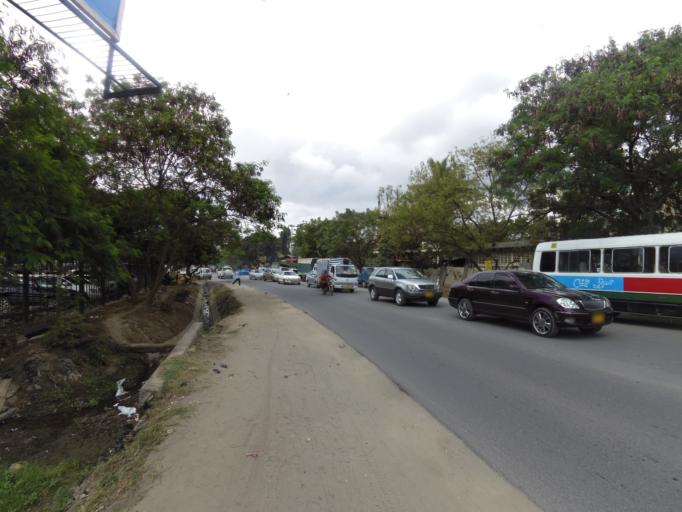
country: TZ
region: Dar es Salaam
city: Magomeni
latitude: -6.7747
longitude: 39.2418
